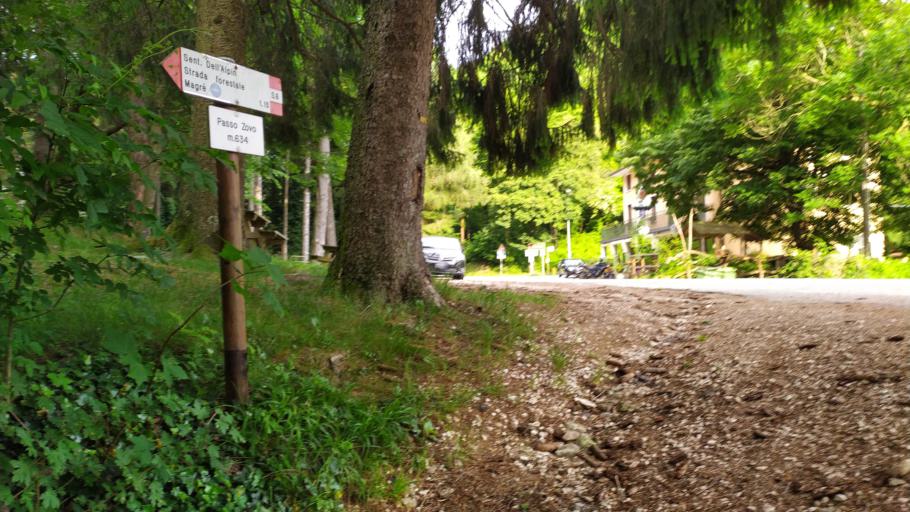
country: IT
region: Veneto
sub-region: Provincia di Vicenza
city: Torrebelvicino
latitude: 45.6842
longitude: 11.3090
